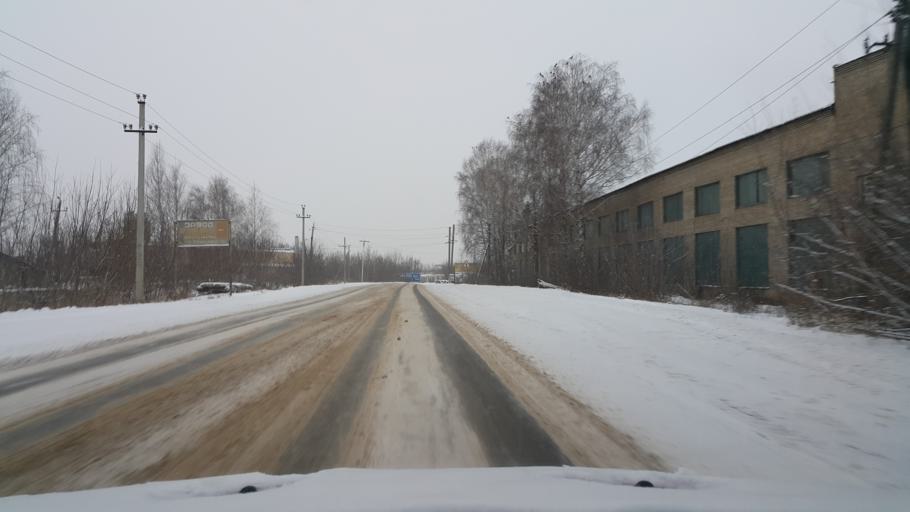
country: RU
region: Tambov
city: Pokrovo-Prigorodnoye
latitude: 52.6568
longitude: 41.4228
